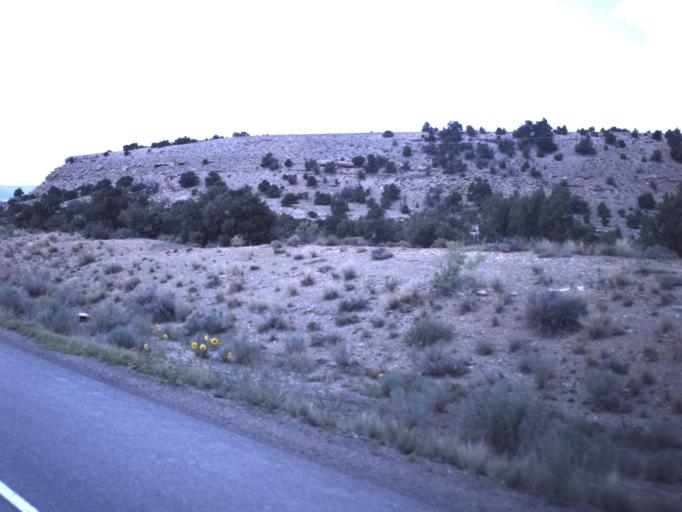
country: US
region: Utah
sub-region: Duchesne County
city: Duchesne
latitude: 40.1666
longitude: -110.4809
